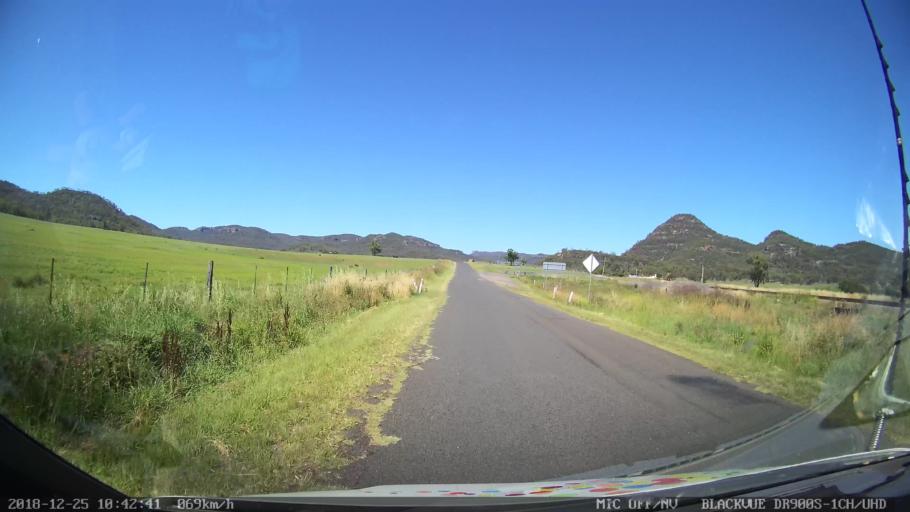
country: AU
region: New South Wales
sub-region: Upper Hunter Shire
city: Merriwa
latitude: -32.4171
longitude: 150.3206
